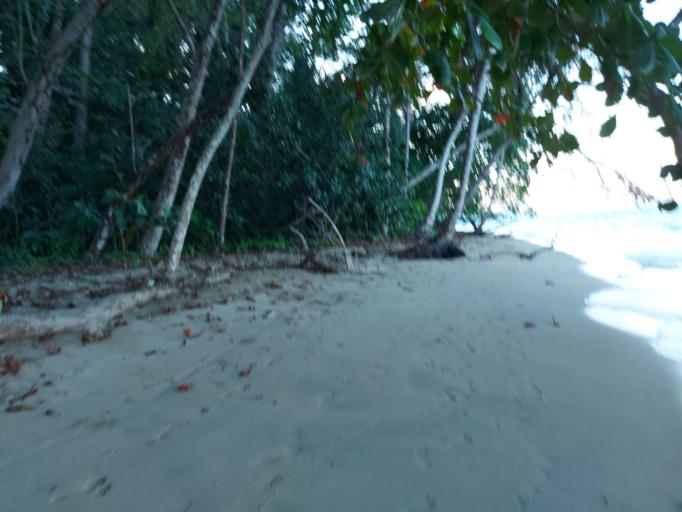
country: PA
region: Bocas del Toro
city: Barranco
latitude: 9.6423
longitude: -82.7128
